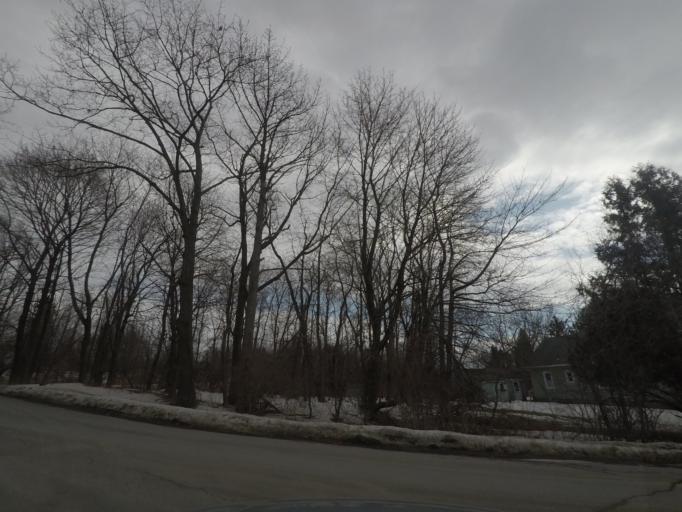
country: US
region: New York
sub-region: Saratoga County
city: Waterford
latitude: 42.7716
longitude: -73.6361
